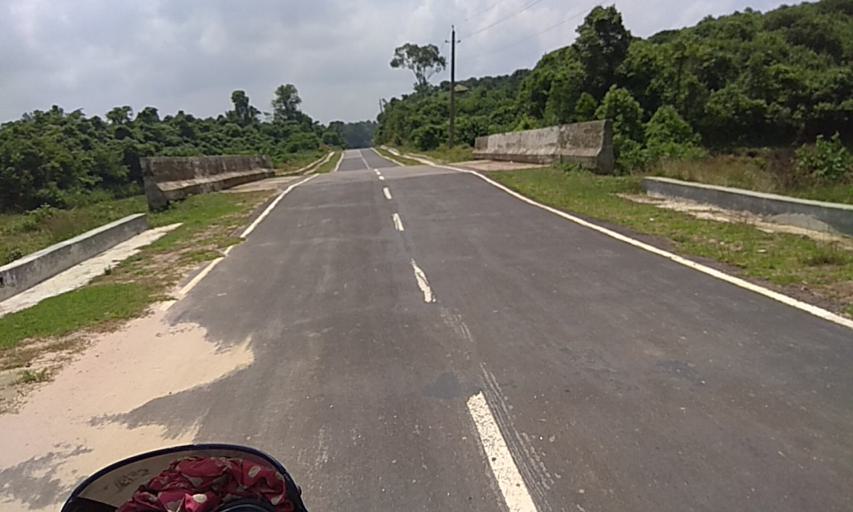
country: BD
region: Chittagong
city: Manikchari
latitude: 22.9376
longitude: 91.9050
